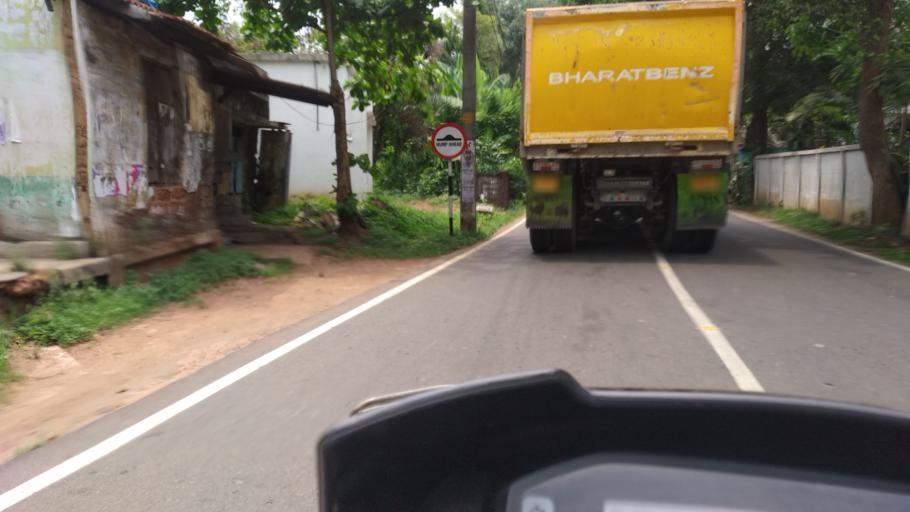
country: IN
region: Kerala
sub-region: Ernakulam
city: Aluva
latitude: 10.1568
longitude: 76.3046
